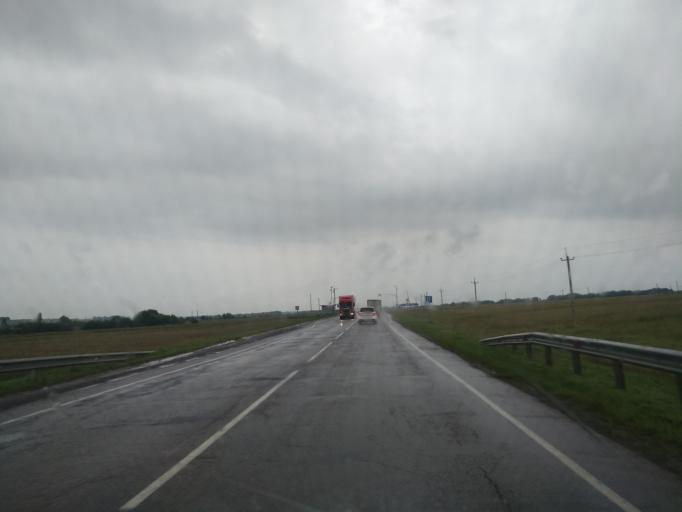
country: RU
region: Voronezj
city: Verkhnyaya Khava
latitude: 51.6780
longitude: 39.8720
